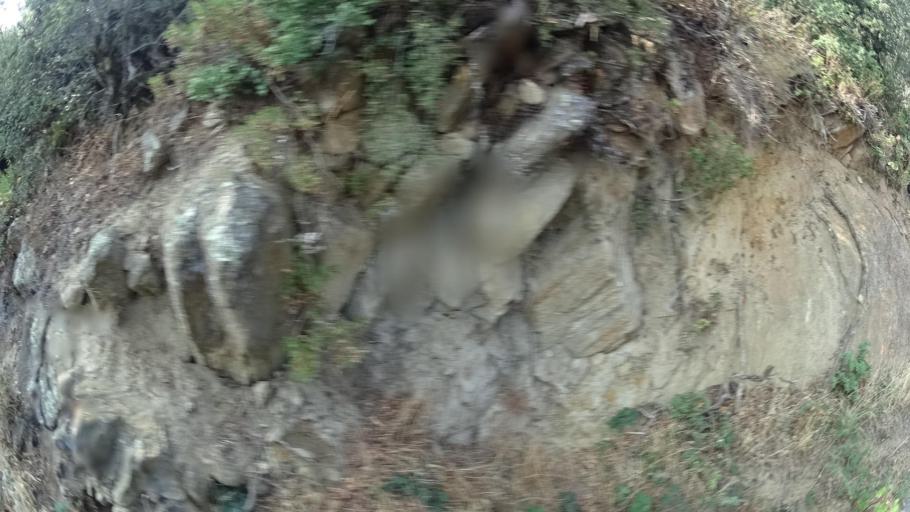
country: US
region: California
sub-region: San Diego County
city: Julian
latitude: 33.0975
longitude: -116.6228
